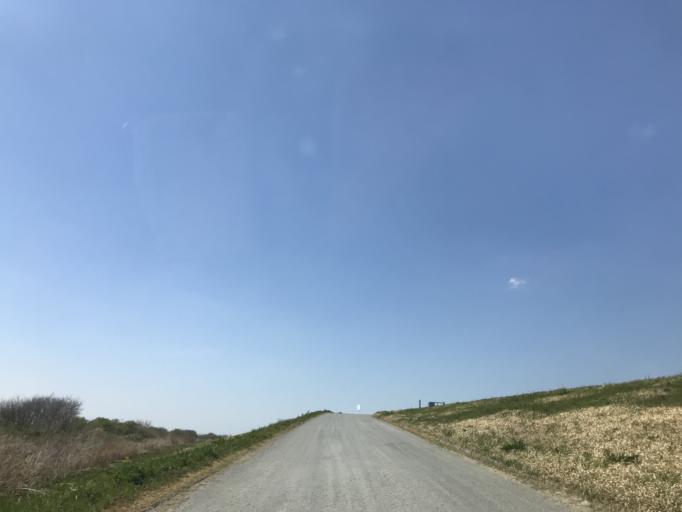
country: JP
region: Ibaraki
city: Moriya
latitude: 35.9154
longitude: 139.9931
